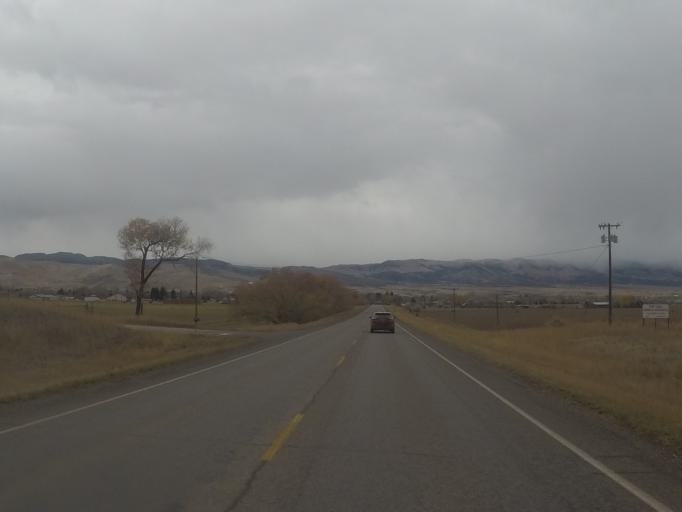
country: US
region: Montana
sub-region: Broadwater County
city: Townsend
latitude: 46.3226
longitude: -111.4990
